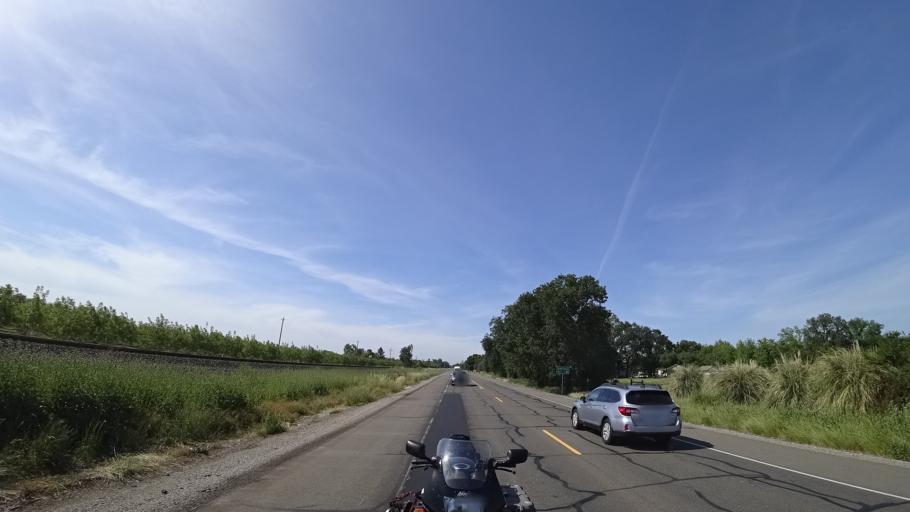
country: US
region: California
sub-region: Tehama County
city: Los Molinos
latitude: 40.0106
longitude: -122.0948
